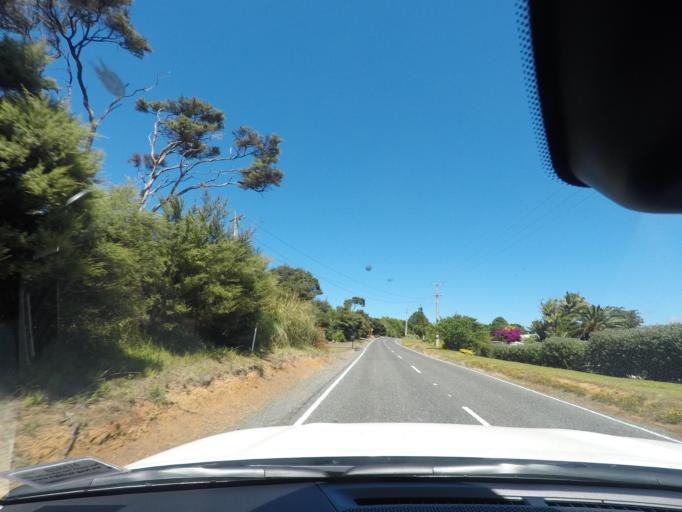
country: NZ
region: Auckland
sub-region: Auckland
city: Parakai
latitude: -36.5767
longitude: 174.3434
